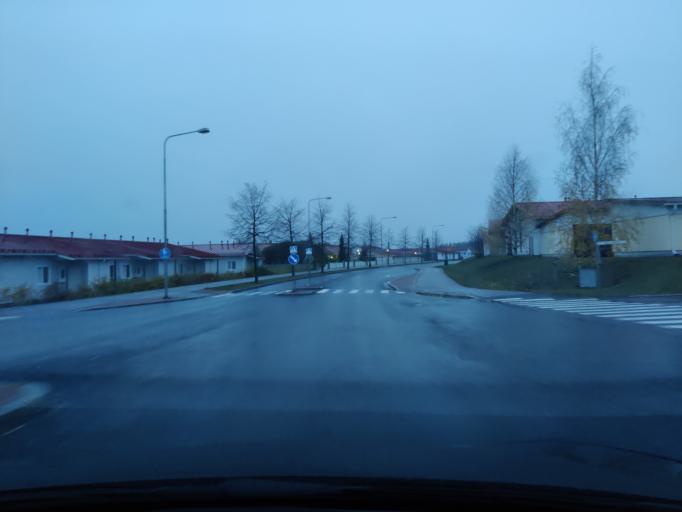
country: FI
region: Northern Savo
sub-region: Kuopio
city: Kuopio
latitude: 62.8270
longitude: 27.6822
